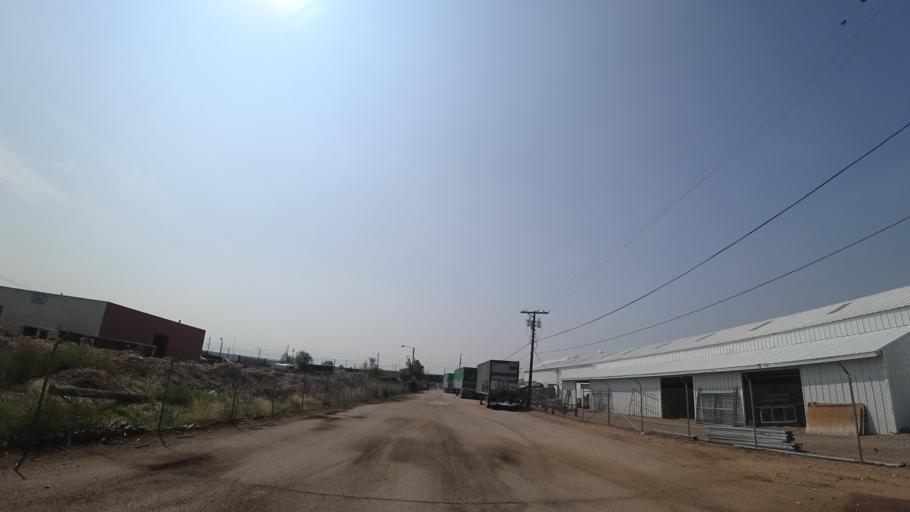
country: US
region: Colorado
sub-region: Arapahoe County
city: Englewood
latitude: 39.6368
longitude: -105.0046
